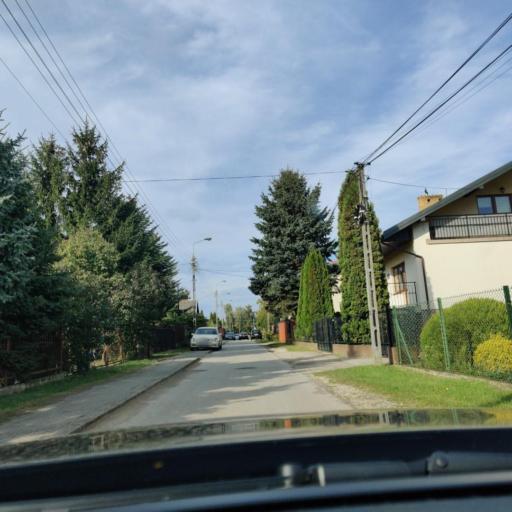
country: PL
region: Lodz Voivodeship
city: Zabia Wola
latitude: 52.0466
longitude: 20.7542
